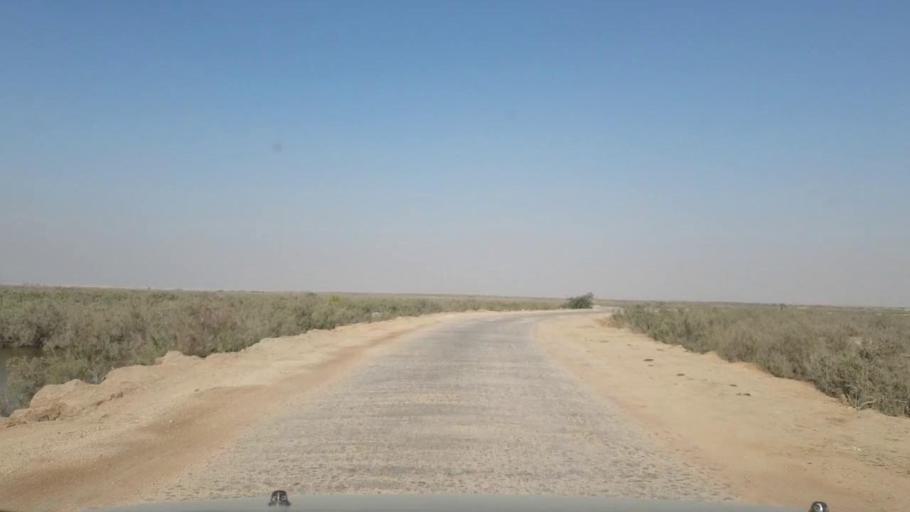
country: PK
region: Sindh
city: Thatta
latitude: 24.8210
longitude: 67.8925
